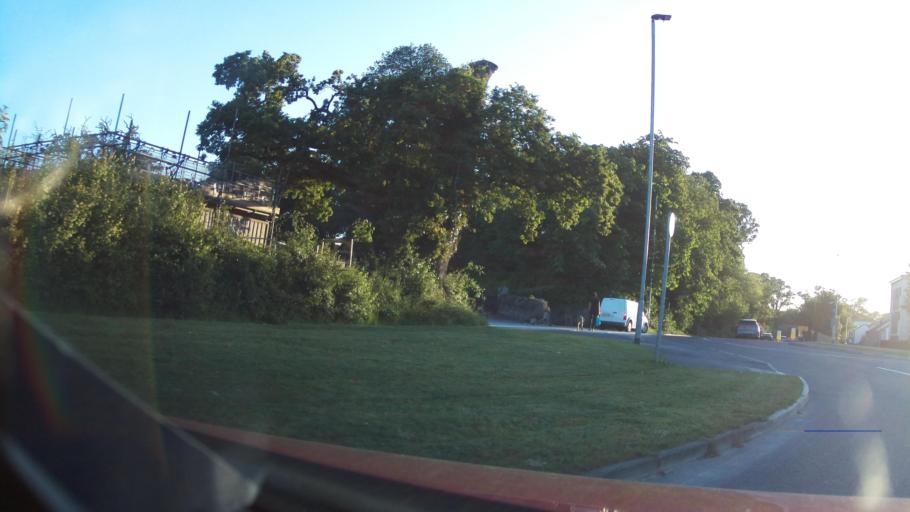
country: GB
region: England
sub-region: Devon
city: Newton Abbot
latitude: 50.5363
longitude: -3.6474
